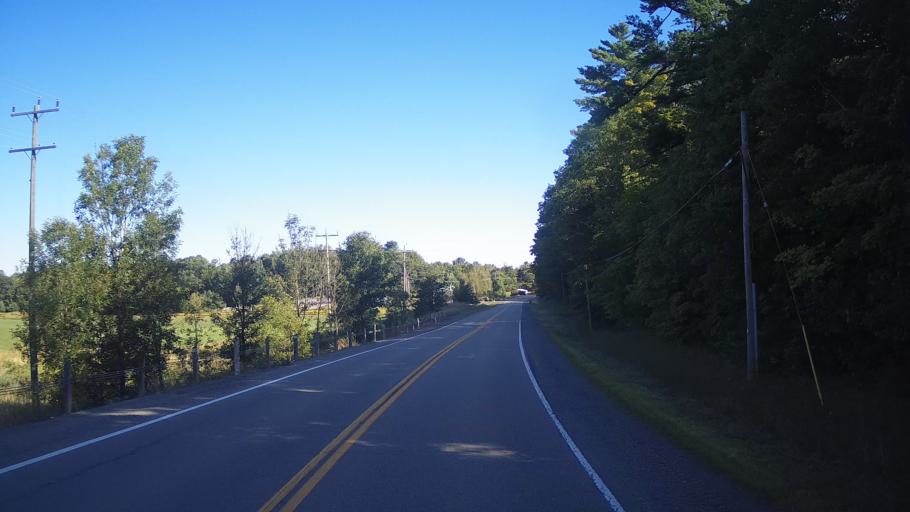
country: CA
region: Ontario
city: Gananoque
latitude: 44.5794
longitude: -76.1117
